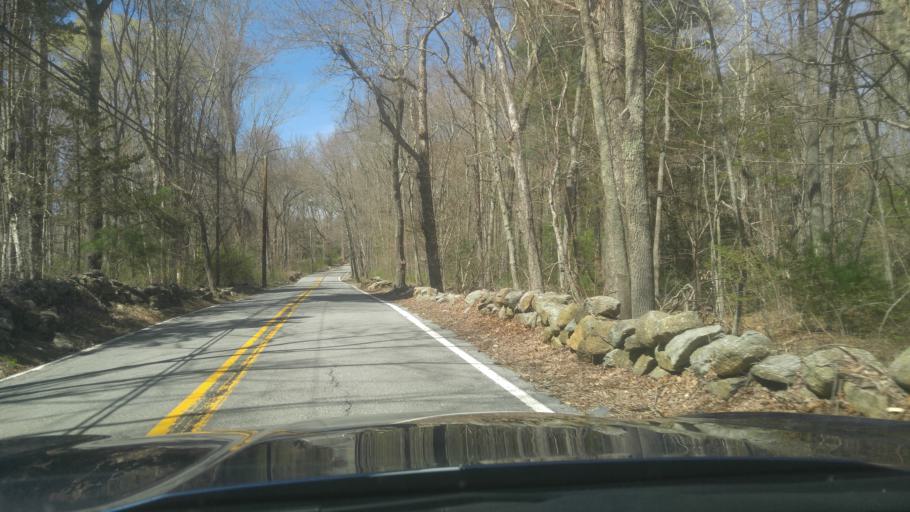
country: US
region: Rhode Island
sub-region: Washington County
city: Hope Valley
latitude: 41.5856
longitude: -71.7581
